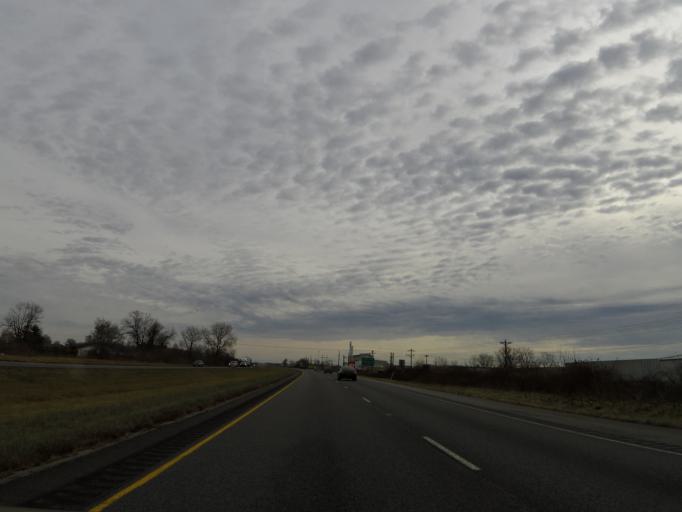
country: US
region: Indiana
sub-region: Hendricks County
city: Pittsboro
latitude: 39.8795
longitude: -86.4991
